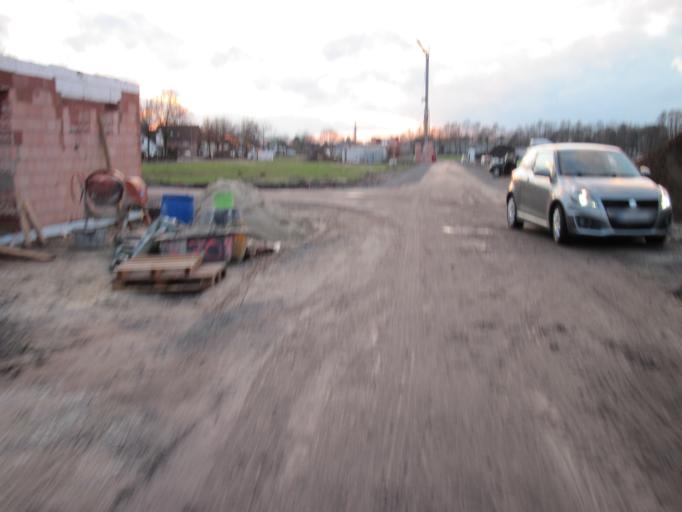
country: DE
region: North Rhine-Westphalia
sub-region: Regierungsbezirk Detmold
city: Hovelhof
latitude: 51.8207
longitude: 8.6774
